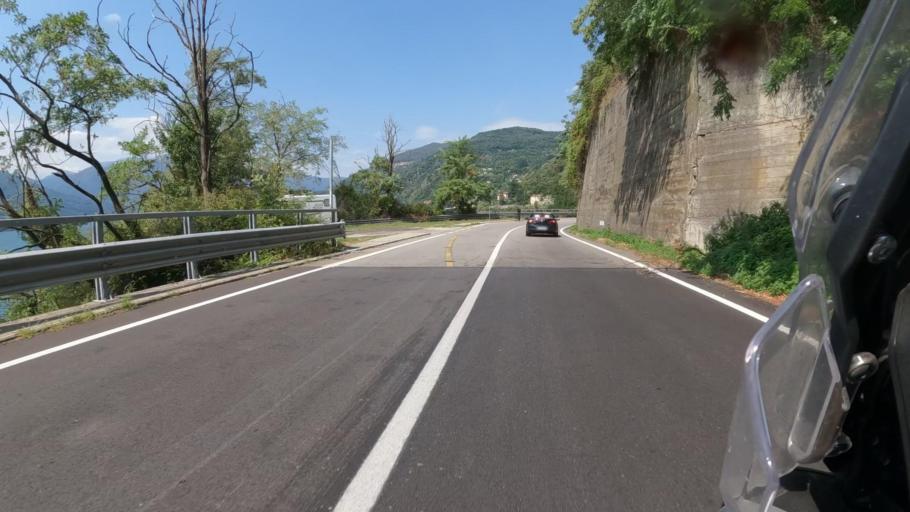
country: IT
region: Lombardy
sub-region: Provincia di Varese
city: Luino
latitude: 46.0128
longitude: 8.7497
